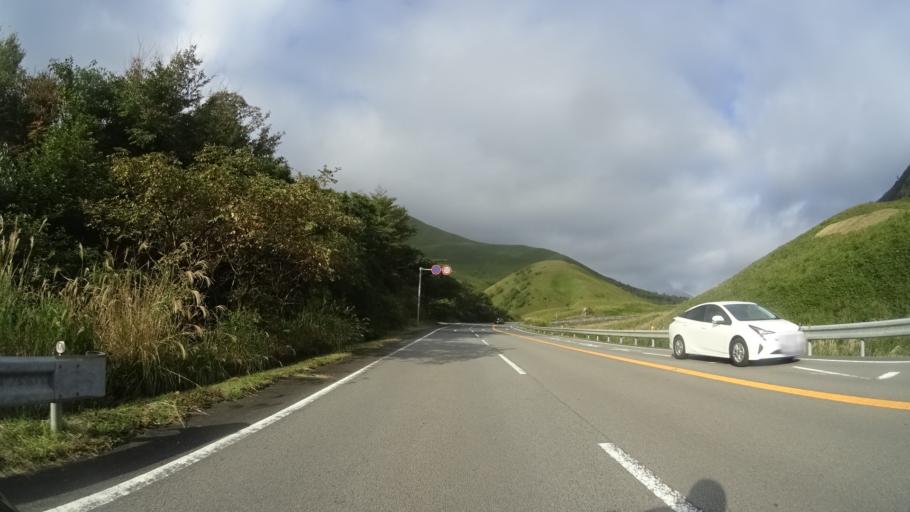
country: JP
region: Oita
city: Beppu
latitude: 33.2605
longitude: 131.3837
